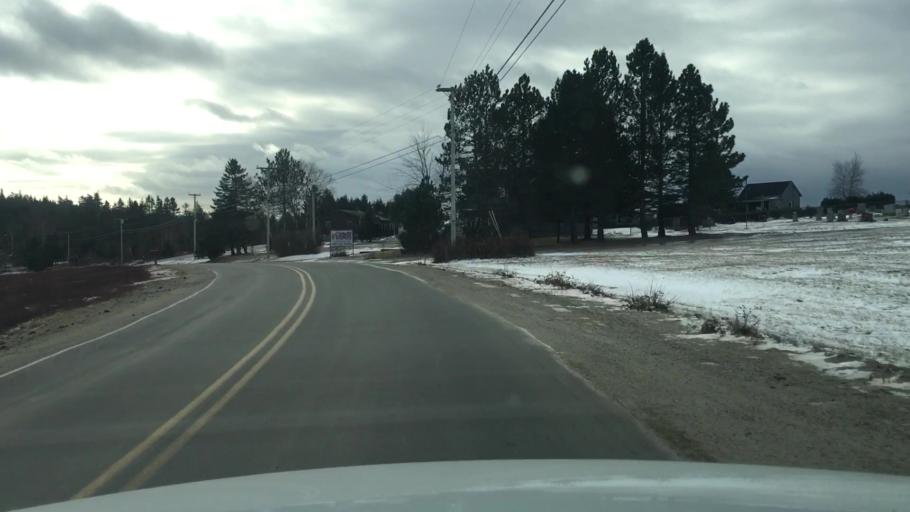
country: US
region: Maine
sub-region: Washington County
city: Jonesport
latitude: 44.6199
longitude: -67.6060
